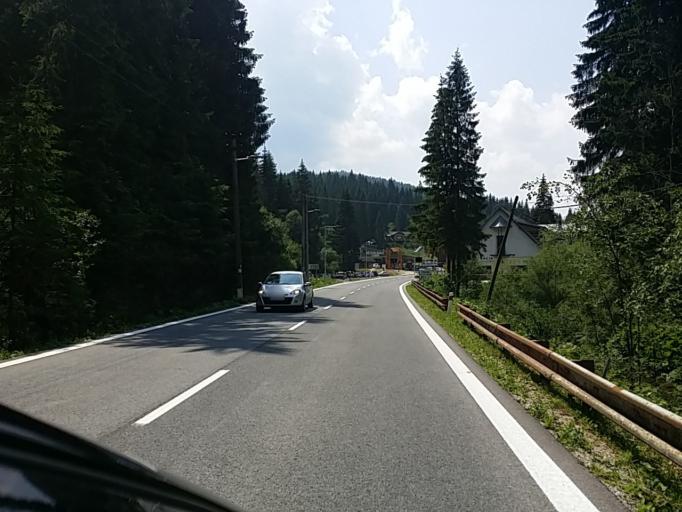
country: SK
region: Kosicky
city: Dobsina
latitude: 48.8748
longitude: 20.3050
